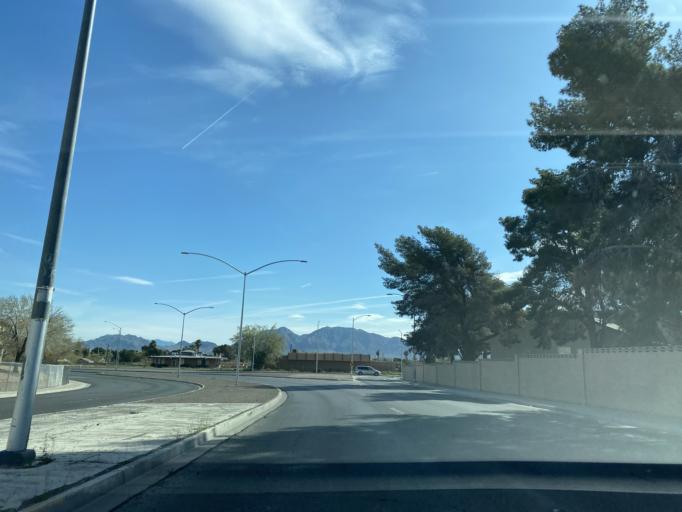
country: US
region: Nevada
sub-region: Clark County
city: Las Vegas
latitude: 36.1781
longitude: -115.1267
